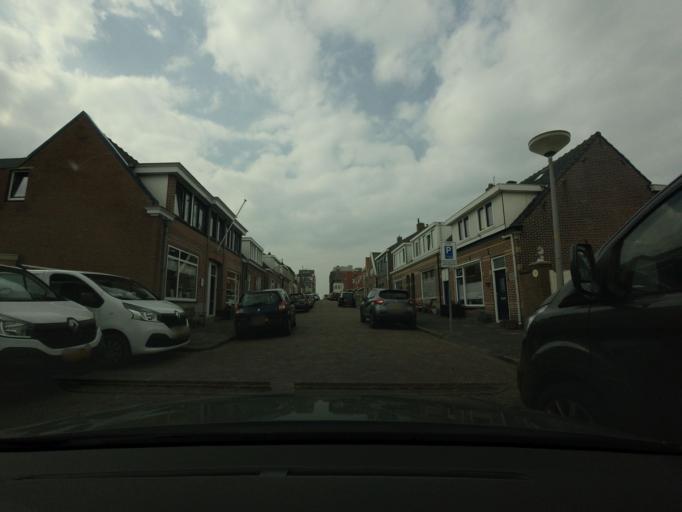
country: NL
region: North Holland
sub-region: Gemeente Bergen
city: Egmond aan Zee
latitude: 52.6203
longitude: 4.6245
